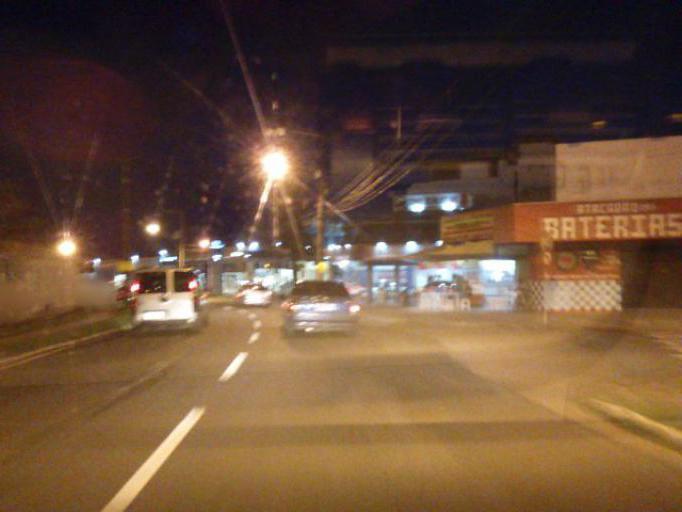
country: BR
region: Santa Catarina
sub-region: Itajai
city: Itajai
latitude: -26.9027
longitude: -48.6688
